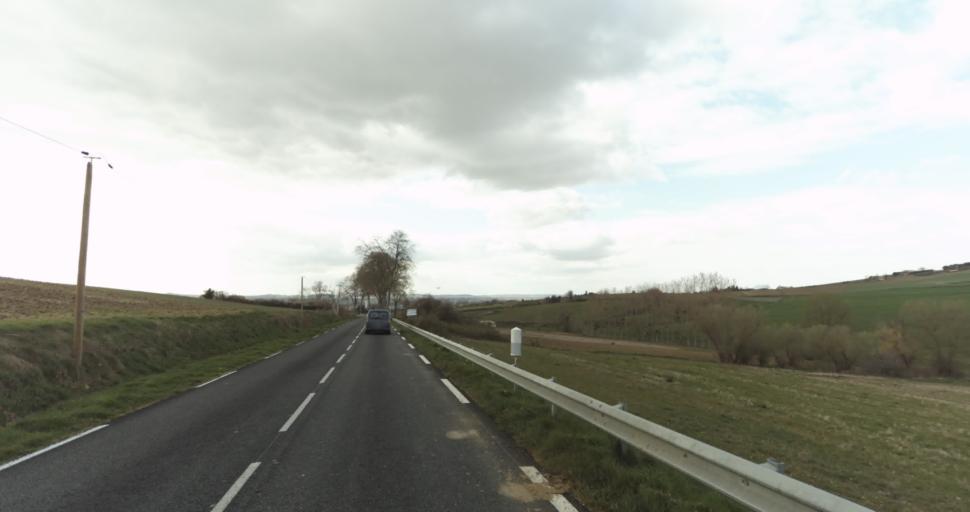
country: FR
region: Midi-Pyrenees
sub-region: Departement de la Haute-Garonne
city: Auterive
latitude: 43.3586
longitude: 1.4902
